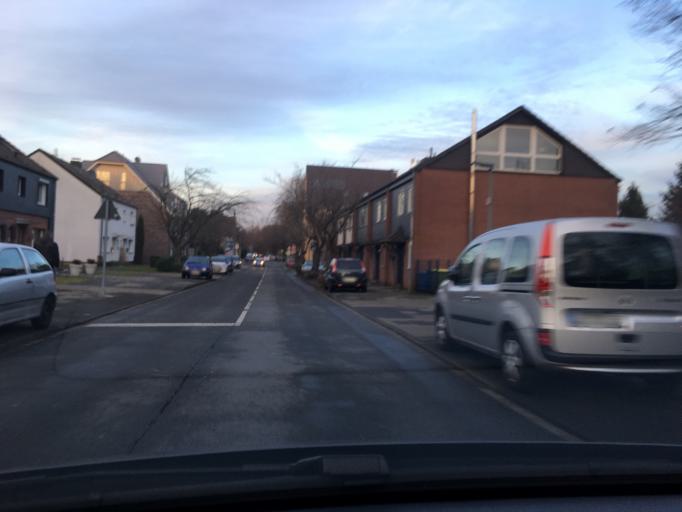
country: DE
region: North Rhine-Westphalia
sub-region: Regierungsbezirk Dusseldorf
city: Oberhausen
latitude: 51.4540
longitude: 6.8377
